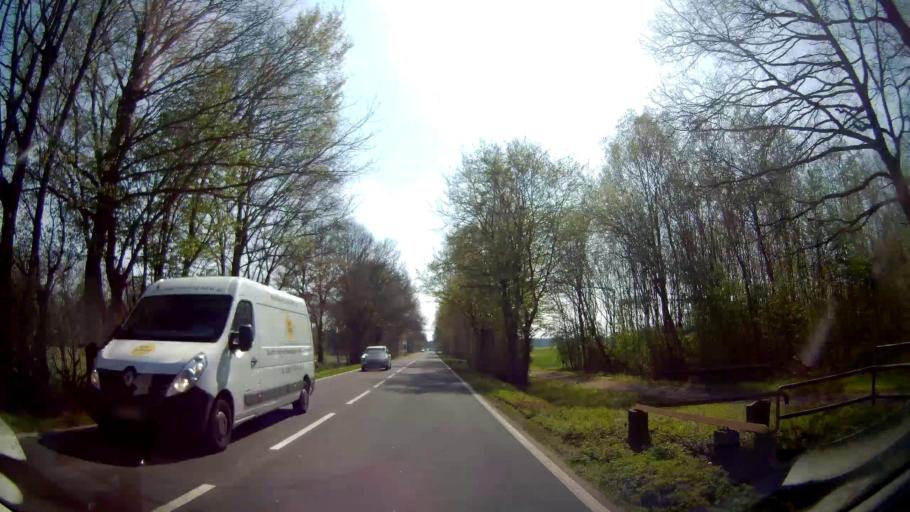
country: DE
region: North Rhine-Westphalia
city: Dorsten
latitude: 51.7011
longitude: 7.0083
